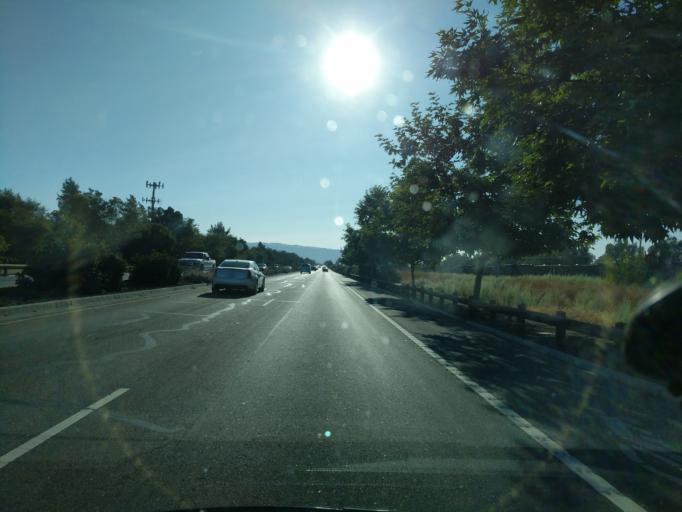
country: US
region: California
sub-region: Alameda County
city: Livermore
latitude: 37.6750
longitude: -121.8162
